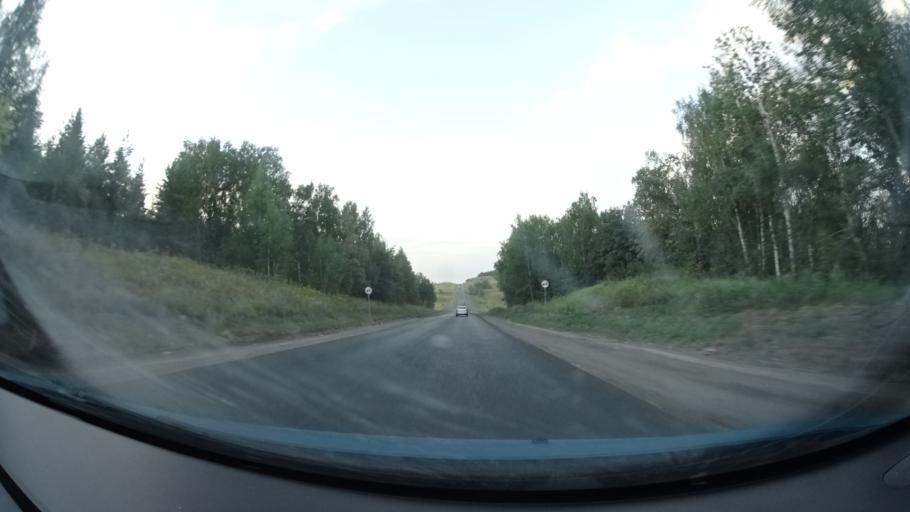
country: RU
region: Orenburg
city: Severnoye
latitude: 54.1640
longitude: 52.6357
